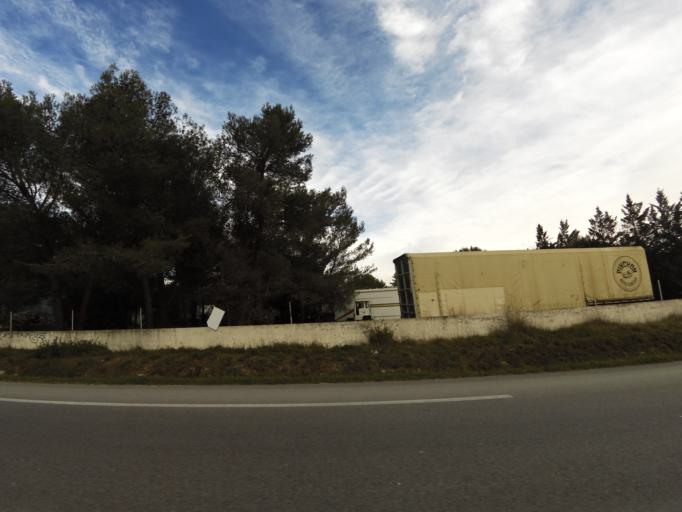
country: FR
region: Languedoc-Roussillon
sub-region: Departement du Gard
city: Milhaud
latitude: 43.8183
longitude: 4.2995
